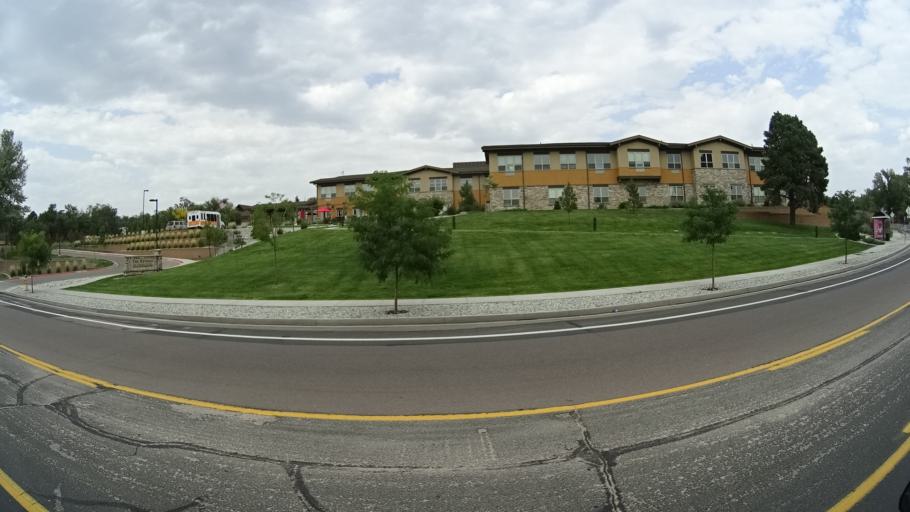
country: US
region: Colorado
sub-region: El Paso County
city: Colorado Springs
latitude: 38.8449
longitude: -104.7834
